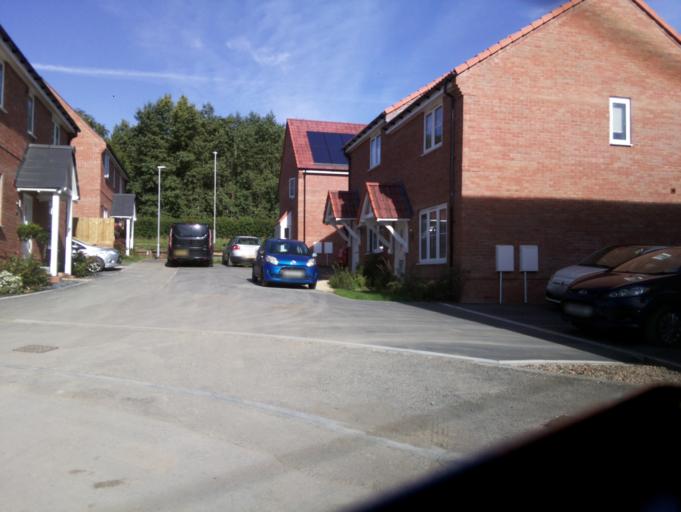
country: GB
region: England
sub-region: Bath and North East Somerset
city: Compton Dando
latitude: 51.3997
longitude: -2.5159
